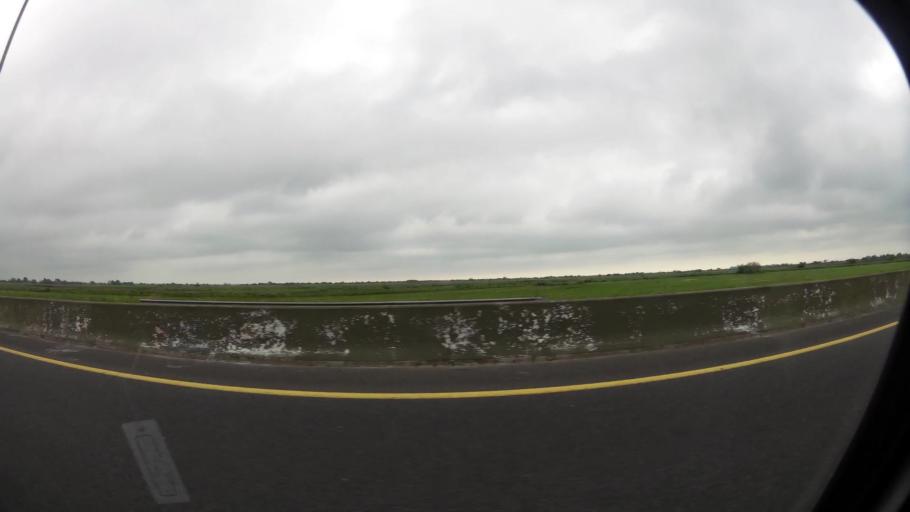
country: AR
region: Buenos Aires
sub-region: Partido de La Plata
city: La Plata
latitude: -34.8423
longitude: -58.0625
